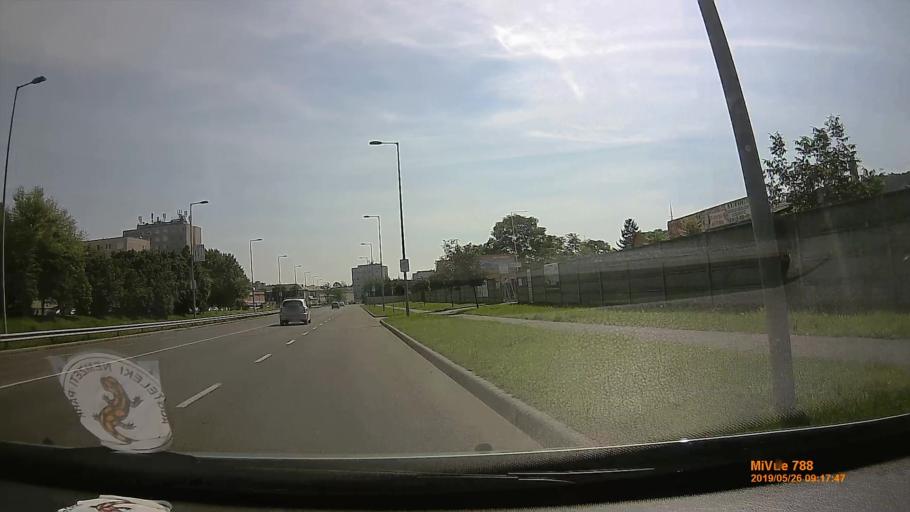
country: HU
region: Borsod-Abauj-Zemplen
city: Miskolc
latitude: 48.1011
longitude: 20.7614
